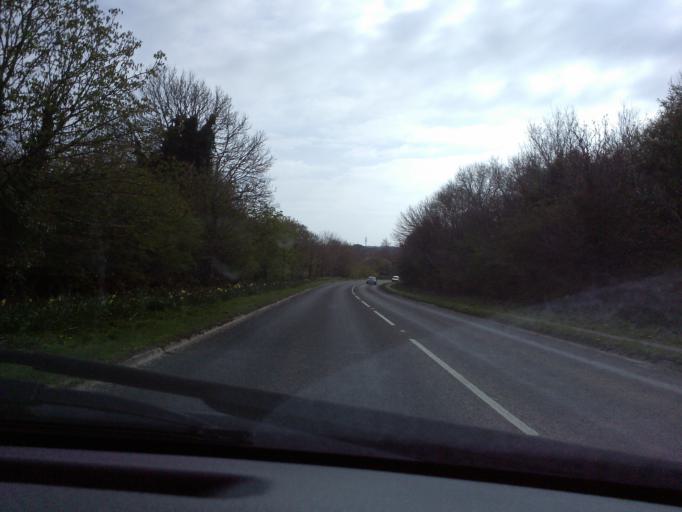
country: GB
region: England
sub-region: Cornwall
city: Penzance
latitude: 50.1225
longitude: -5.5502
